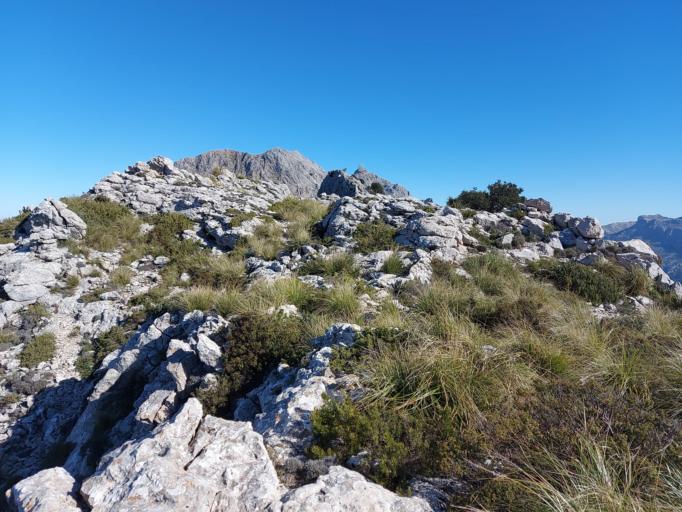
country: ES
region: Balearic Islands
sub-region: Illes Balears
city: Fornalutx
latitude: 39.7837
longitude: 2.7707
